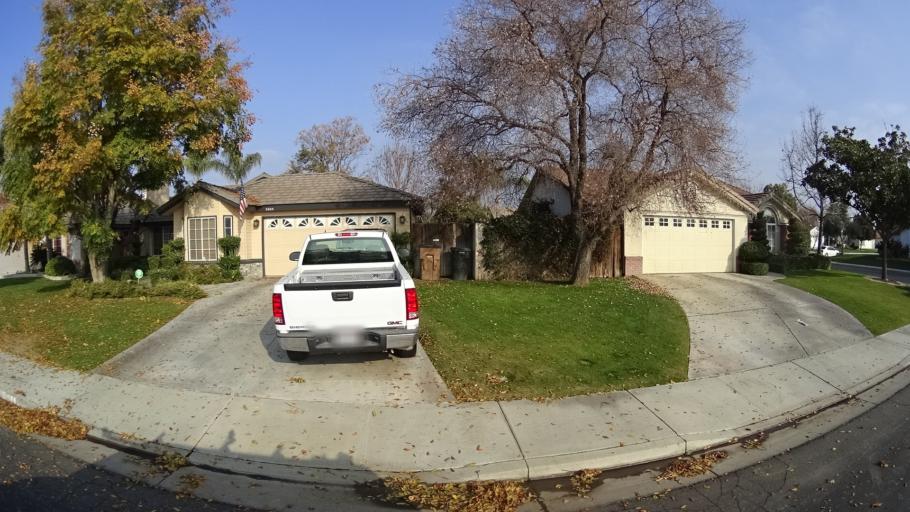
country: US
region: California
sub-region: Kern County
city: Greenfield
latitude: 35.2988
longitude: -119.0649
